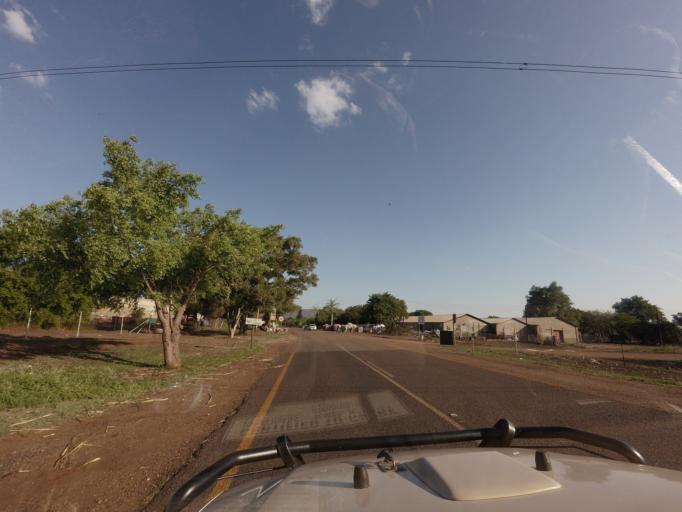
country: ZA
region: Mpumalanga
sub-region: Ehlanzeni District
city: Komatipoort
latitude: -25.4275
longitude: 31.9472
